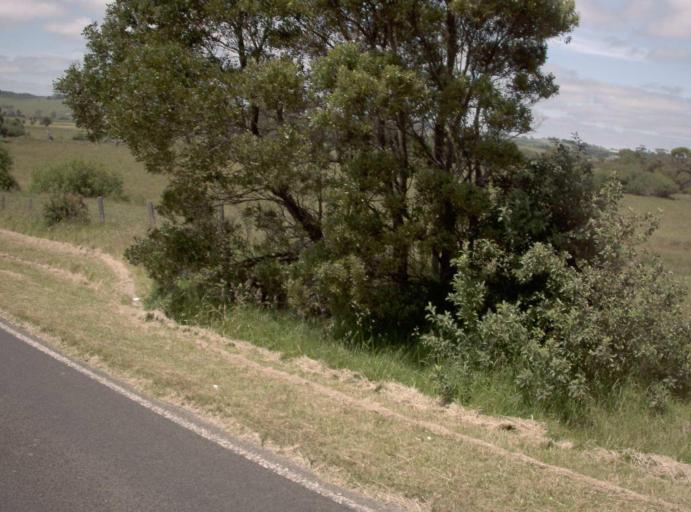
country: AU
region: Victoria
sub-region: Baw Baw
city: Warragul
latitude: -38.4786
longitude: 145.9713
